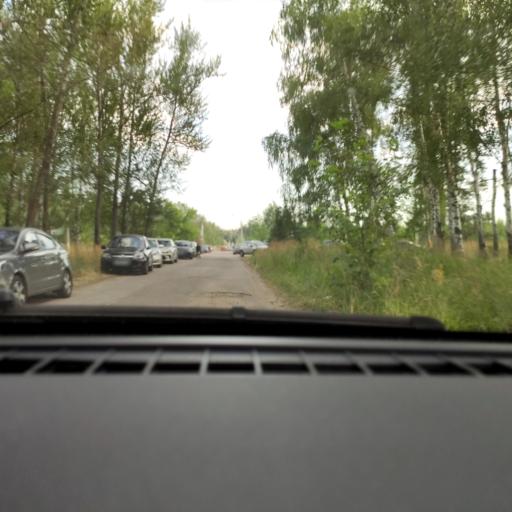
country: RU
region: Voronezj
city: Somovo
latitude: 51.7324
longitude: 39.3196
